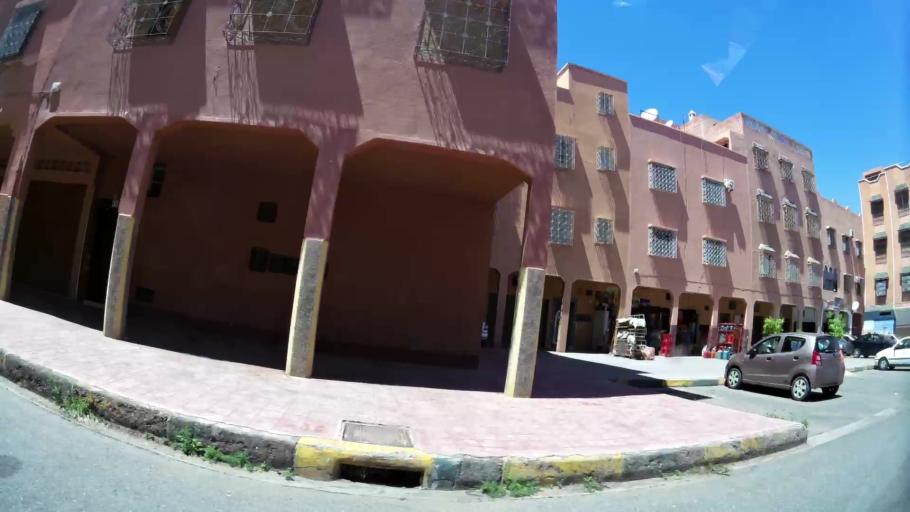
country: MA
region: Marrakech-Tensift-Al Haouz
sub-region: Marrakech
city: Marrakesh
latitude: 31.6310
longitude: -8.0543
